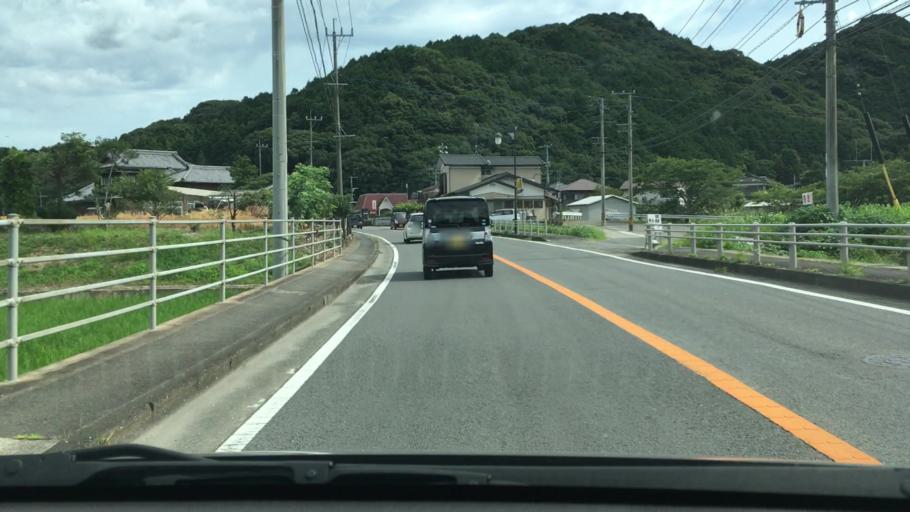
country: JP
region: Nagasaki
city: Togitsu
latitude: 32.8938
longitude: 129.7805
